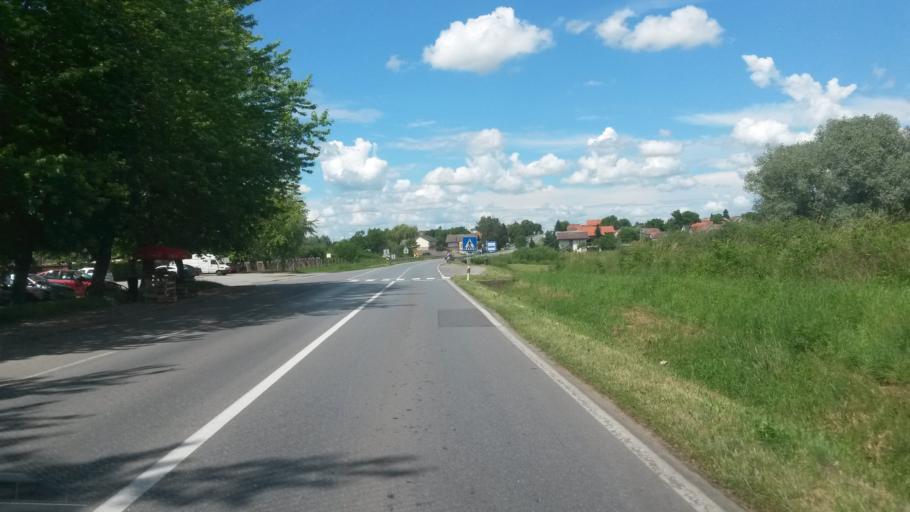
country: HR
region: Osjecko-Baranjska
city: Viskovci
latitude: 45.3422
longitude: 18.4210
